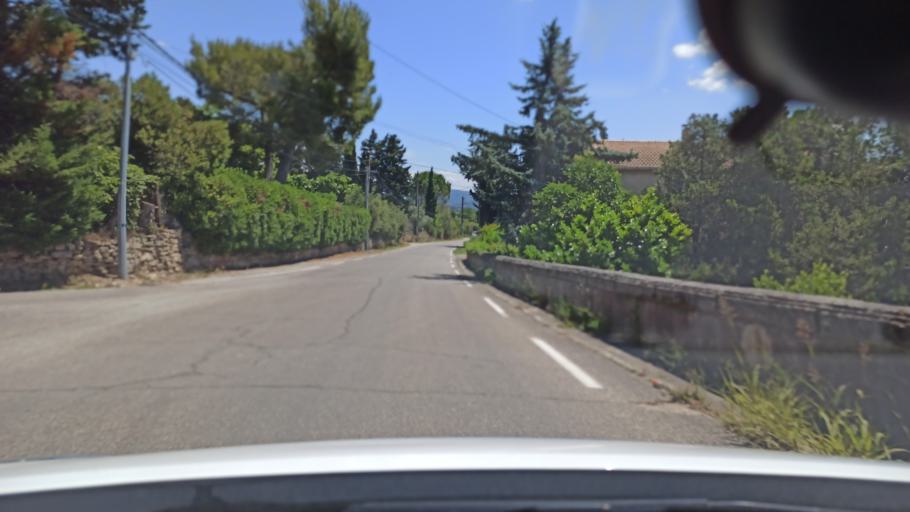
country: FR
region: Provence-Alpes-Cote d'Azur
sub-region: Departement du Vaucluse
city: Caumont-sur-Durance
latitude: 43.8981
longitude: 4.9371
